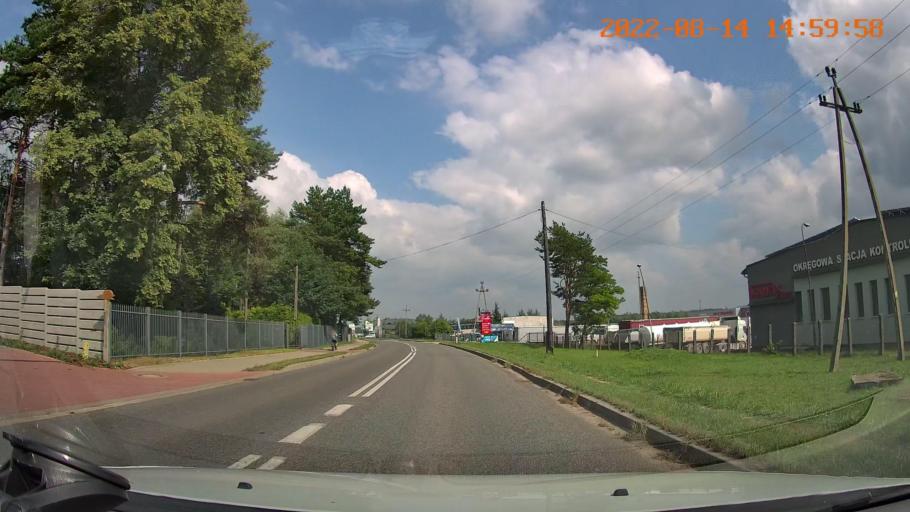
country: PL
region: Swietokrzyskie
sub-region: Powiat kielecki
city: Piekoszow
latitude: 50.8811
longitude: 20.4881
